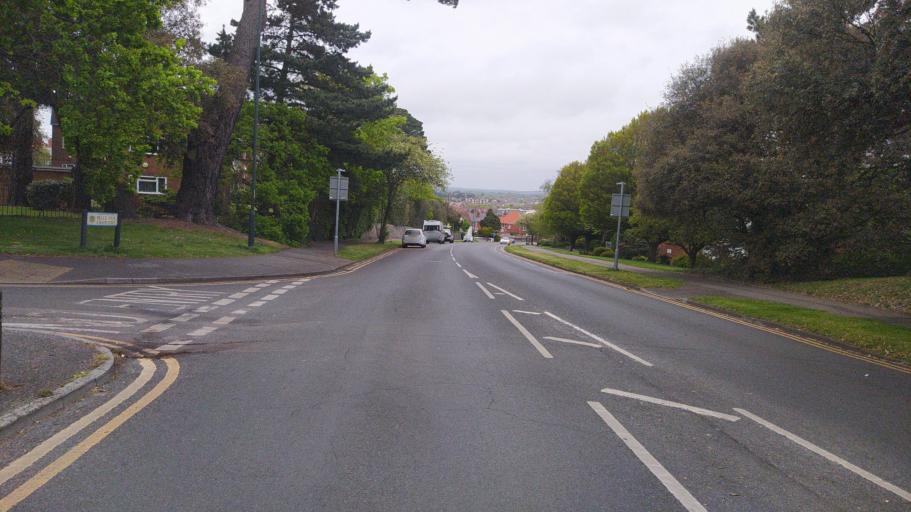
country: GB
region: England
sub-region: Dorset
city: Christchurch
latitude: 50.7240
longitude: -1.7945
